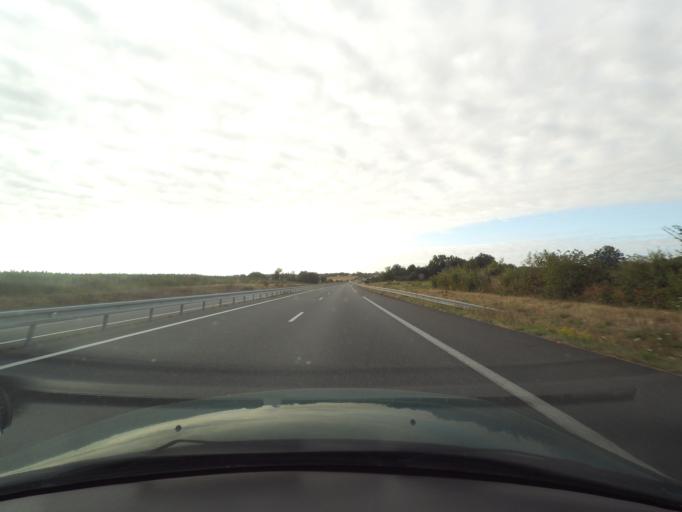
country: FR
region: Poitou-Charentes
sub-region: Departement des Deux-Sevres
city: Saint-Pierre-des-Echaubrognes
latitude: 46.9619
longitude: -0.7873
